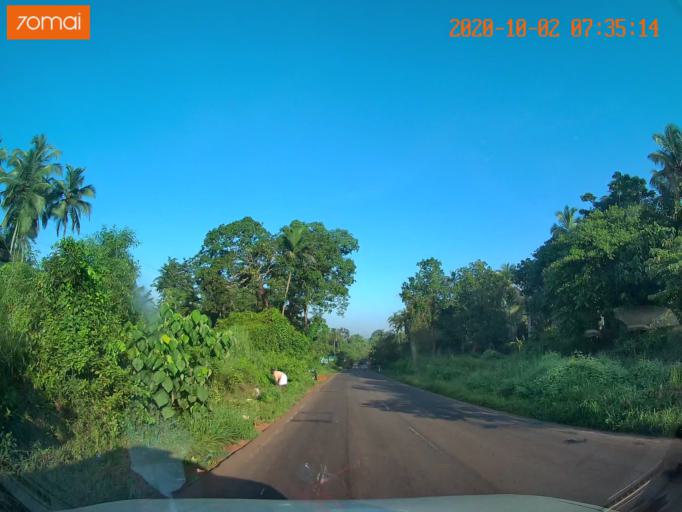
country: IN
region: Kerala
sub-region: Malappuram
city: Pariyapuram
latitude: 11.0681
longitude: 75.9218
